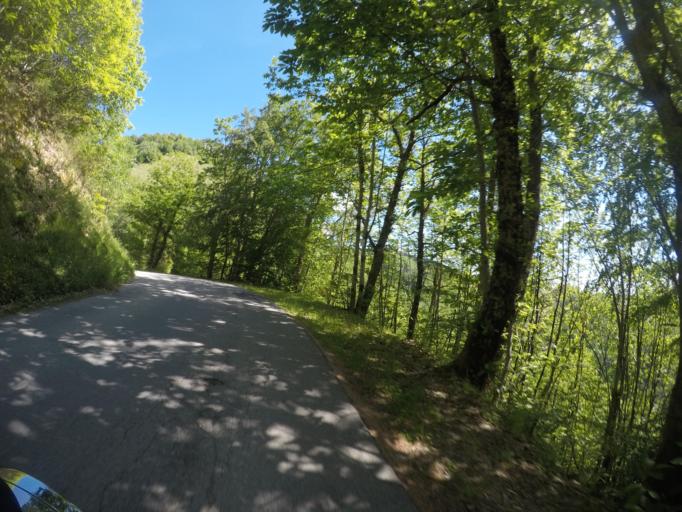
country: IT
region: Tuscany
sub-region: Provincia di Lucca
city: Careggine
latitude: 44.0941
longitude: 10.3245
